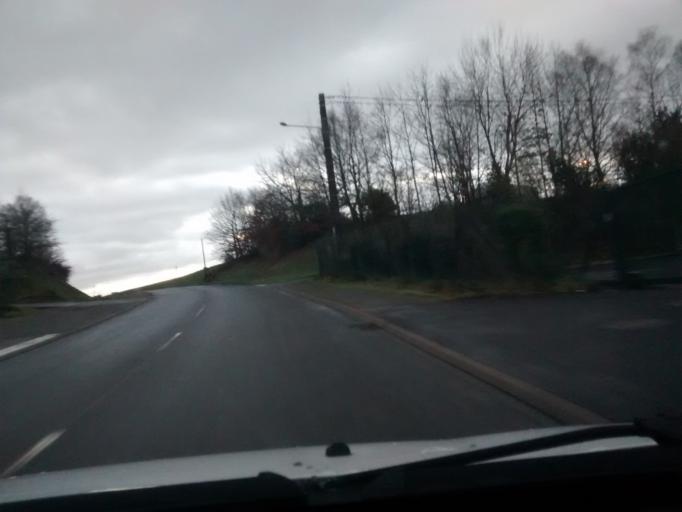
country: FR
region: Brittany
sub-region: Departement d'Ille-et-Vilaine
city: Chateaubourg
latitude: 48.1021
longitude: -1.4140
